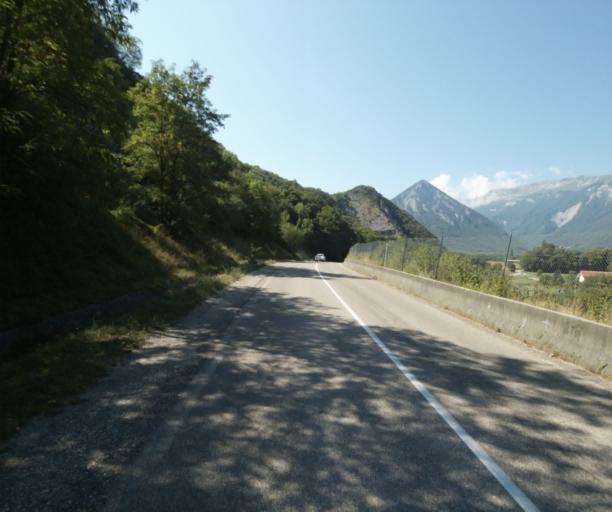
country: FR
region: Rhone-Alpes
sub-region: Departement de l'Isere
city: Allieres-et-Risset
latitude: 45.0846
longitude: 5.6764
